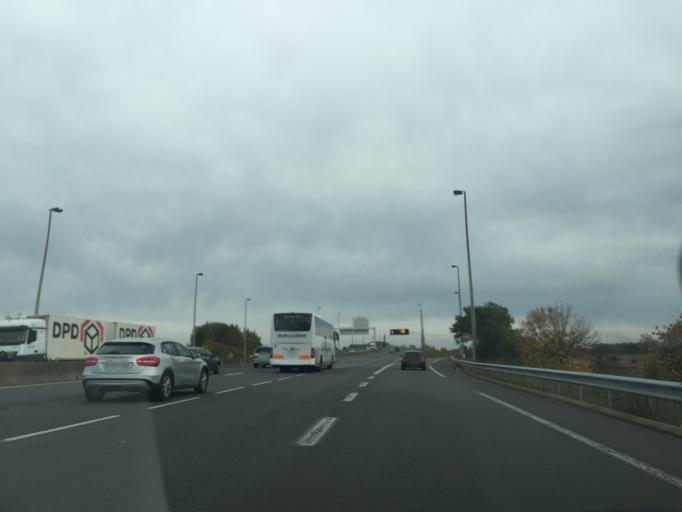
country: FR
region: Nord-Pas-de-Calais
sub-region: Departement du Pas-de-Calais
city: Frethun
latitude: 50.9404
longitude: 1.8316
